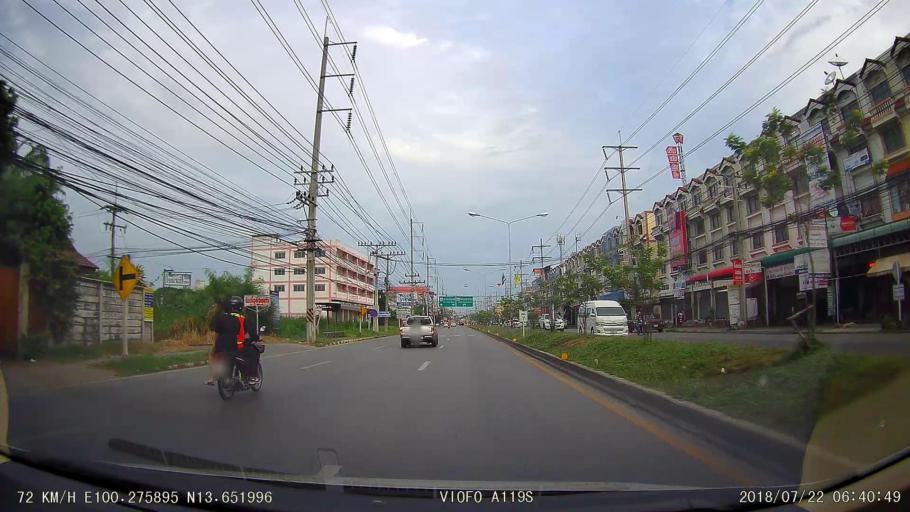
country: TH
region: Samut Sakhon
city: Krathum Baen
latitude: 13.6521
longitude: 100.2757
